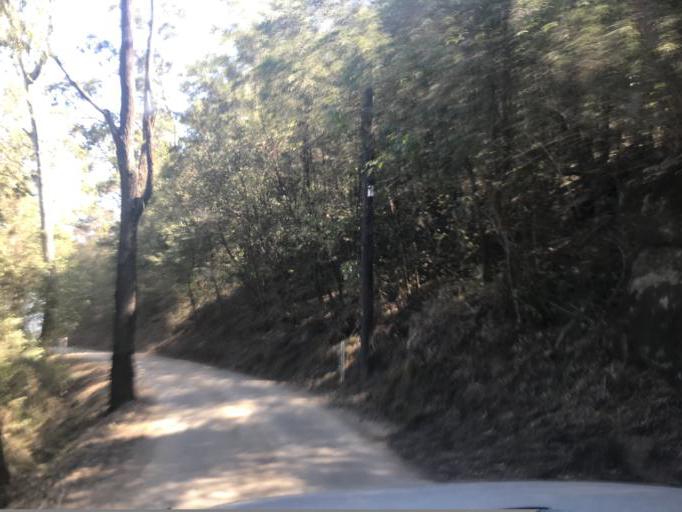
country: AU
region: New South Wales
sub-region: Hawkesbury
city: Pitt Town
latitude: -33.4180
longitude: 150.9070
